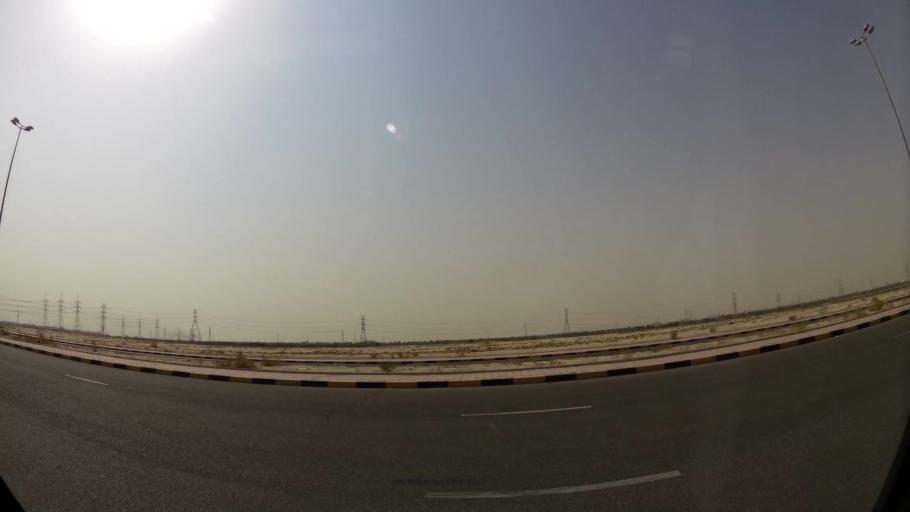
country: KW
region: Muhafazat al Jahra'
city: Al Jahra'
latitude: 29.3235
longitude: 47.7777
